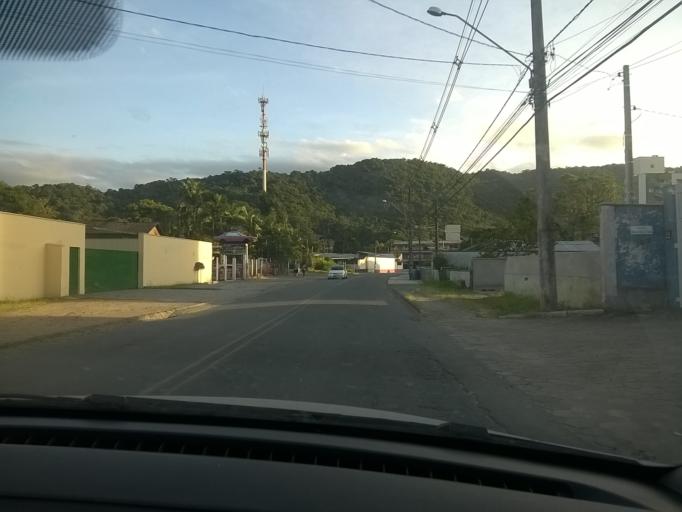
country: BR
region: Santa Catarina
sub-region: Blumenau
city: Blumenau
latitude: -26.9317
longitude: -49.1351
